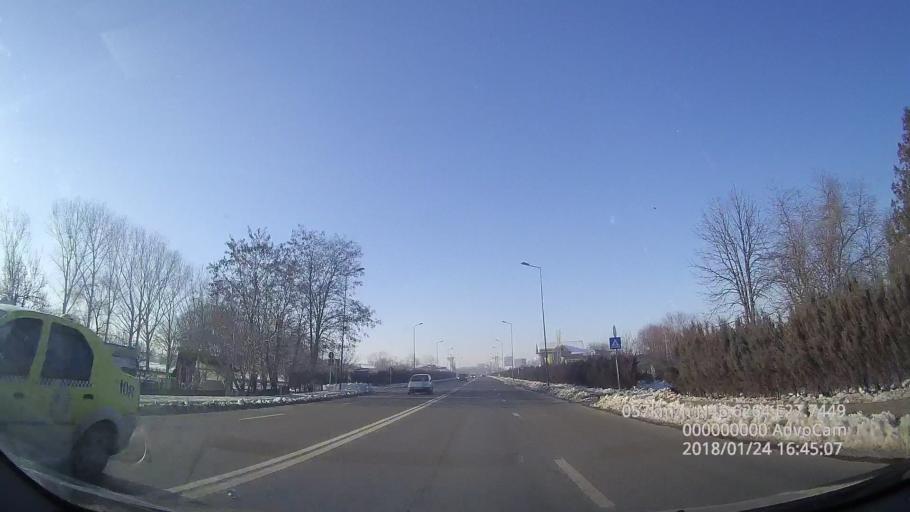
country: RO
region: Vaslui
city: Vaslui
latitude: 46.6266
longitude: 27.7444
